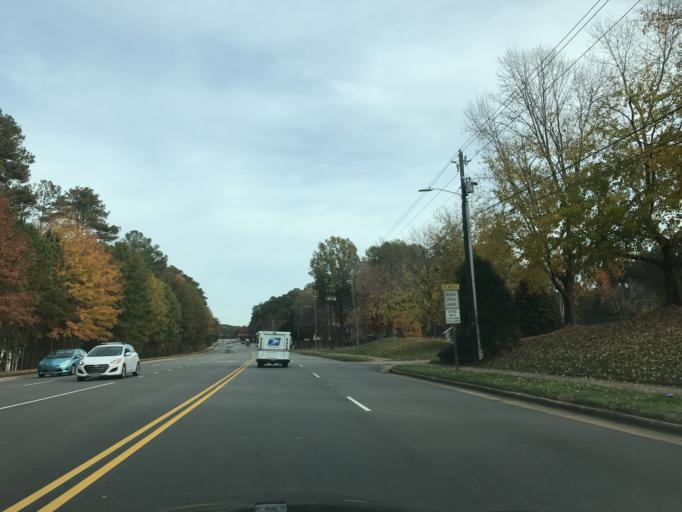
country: US
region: North Carolina
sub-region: Wake County
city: West Raleigh
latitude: 35.8947
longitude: -78.6386
